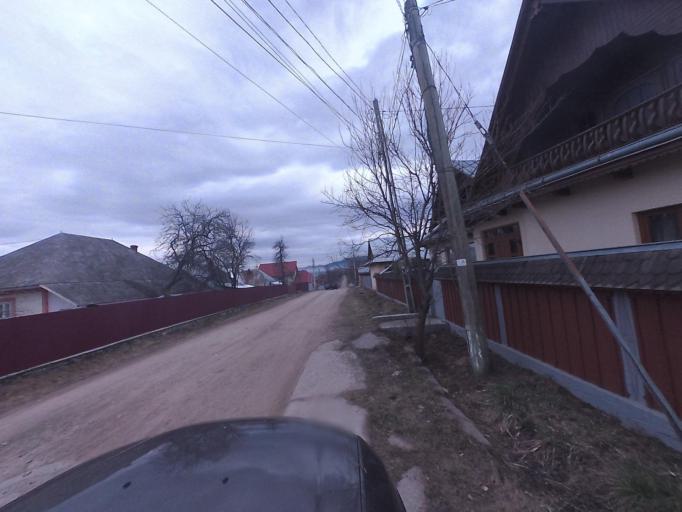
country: RO
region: Neamt
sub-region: Oras Targu Neamt
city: Humulesti
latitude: 47.1899
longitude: 26.3386
